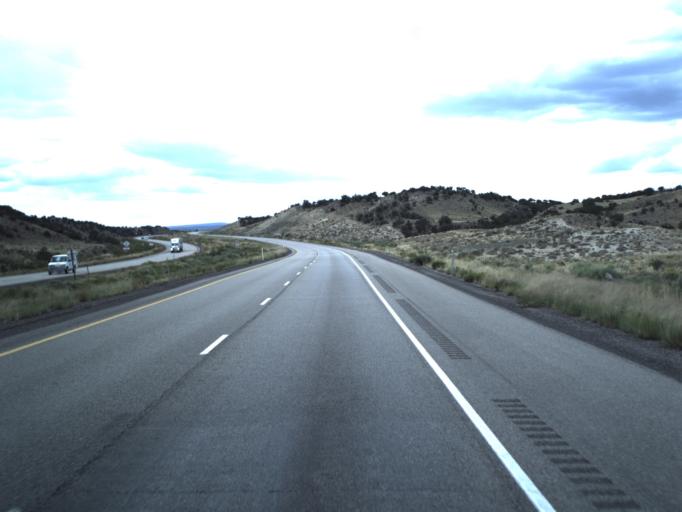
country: US
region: Utah
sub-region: Emery County
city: Ferron
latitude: 38.7905
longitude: -111.2967
